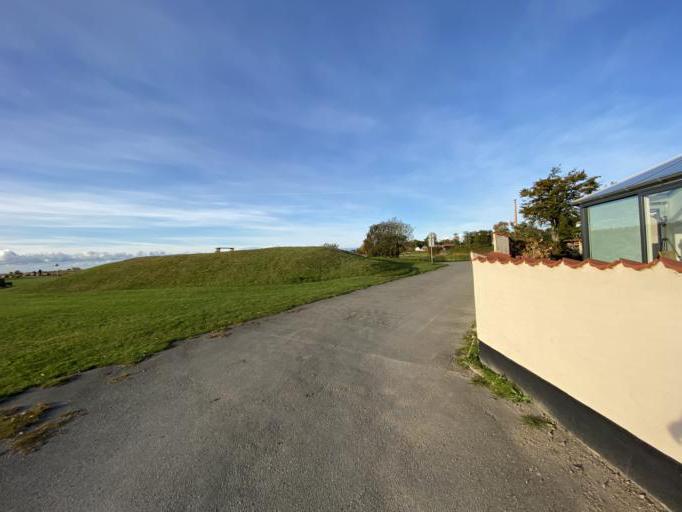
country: DK
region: Capital Region
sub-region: Dragor Kommune
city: Dragor
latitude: 55.5895
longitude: 12.6728
